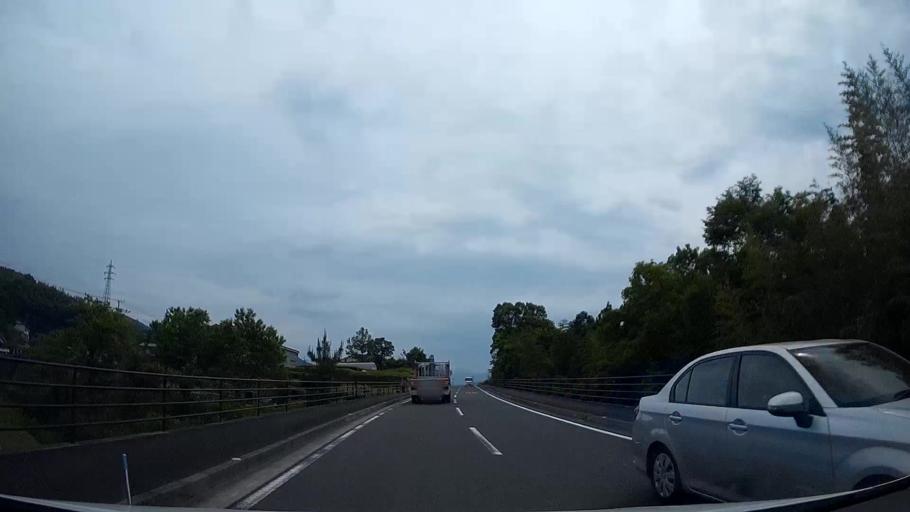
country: JP
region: Shizuoka
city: Ito
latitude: 34.9664
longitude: 138.9470
